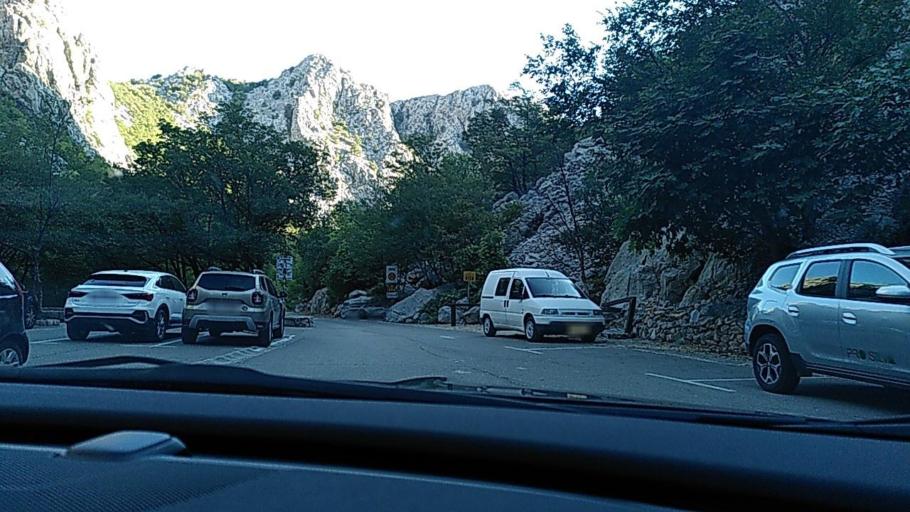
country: HR
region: Zadarska
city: Starigrad
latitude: 44.3028
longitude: 15.4709
